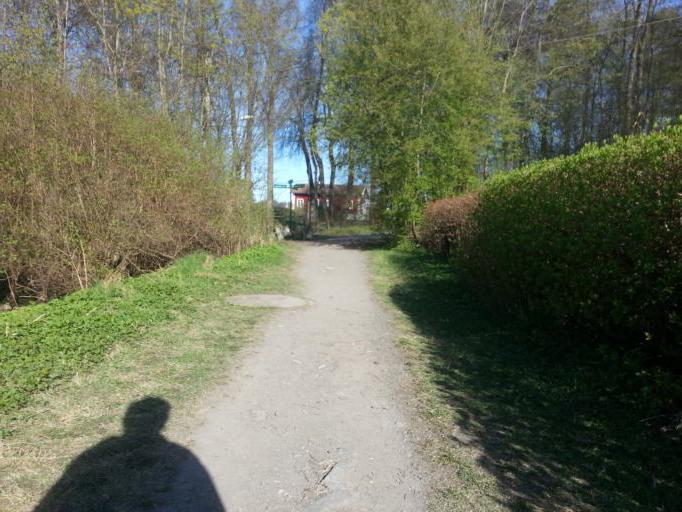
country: NO
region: Oslo
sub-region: Oslo
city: Sjolyststranda
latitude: 59.9145
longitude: 10.6723
